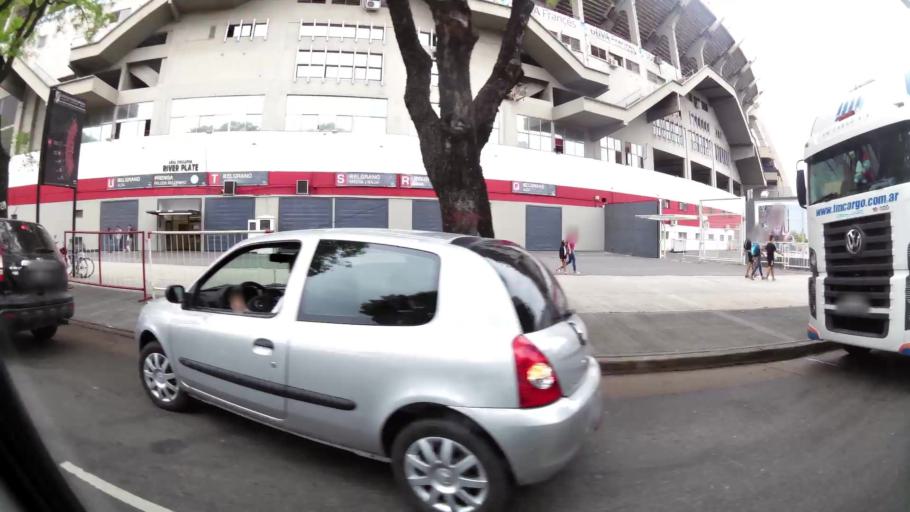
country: AR
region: Buenos Aires F.D.
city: Colegiales
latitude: -34.5453
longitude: -58.4512
